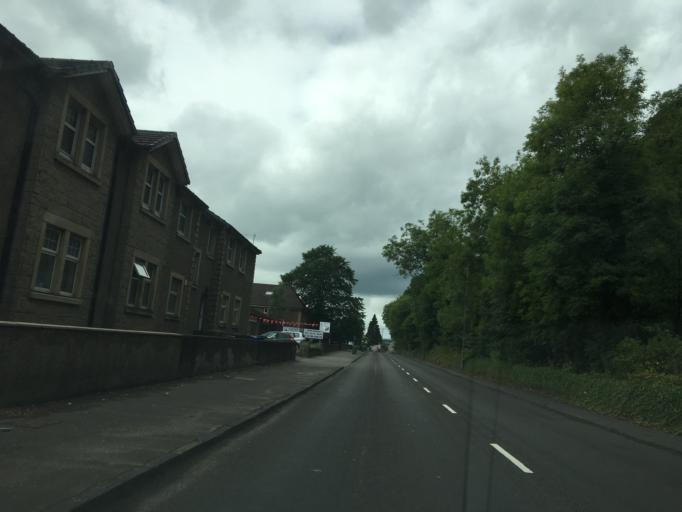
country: GB
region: Scotland
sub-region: Stirling
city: Stirling
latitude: 56.1352
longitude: -3.9160
